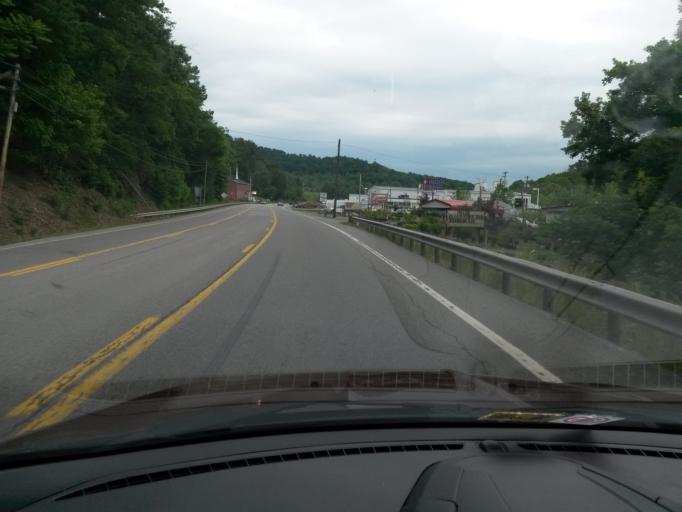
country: US
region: West Virginia
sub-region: Lewis County
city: Weston
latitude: 39.0334
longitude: -80.4436
